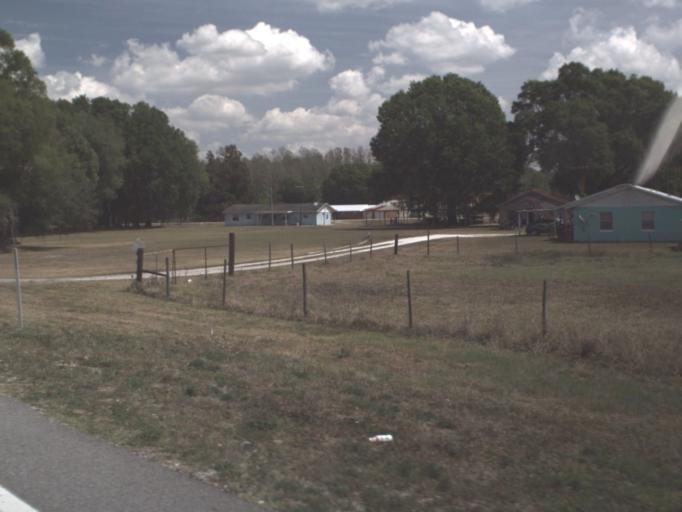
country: US
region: Florida
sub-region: Hernando County
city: Ridge Manor
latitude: 28.5505
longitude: -82.0896
